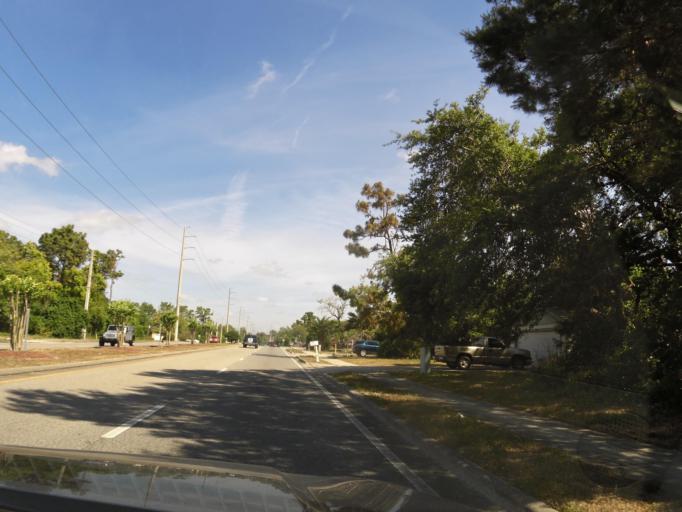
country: US
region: Florida
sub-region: Volusia County
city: Deltona
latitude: 28.9126
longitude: -81.1815
